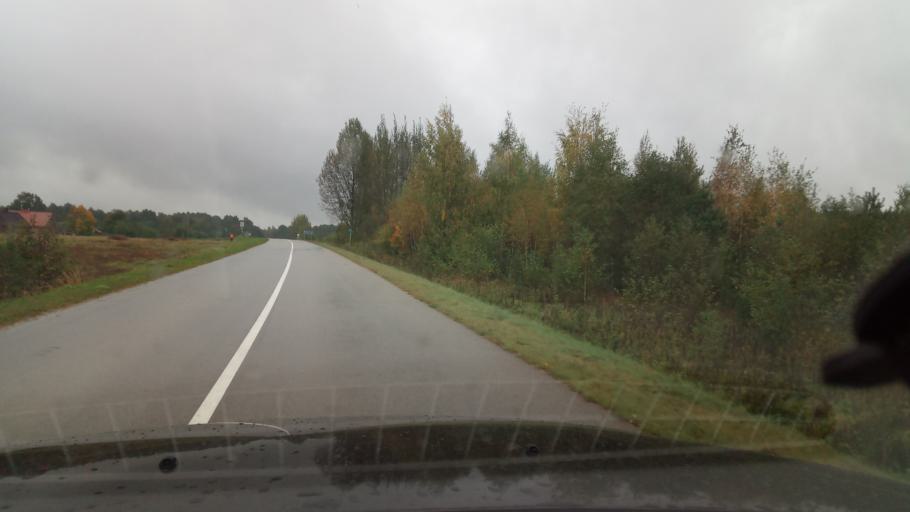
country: LT
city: Skaidiskes
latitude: 54.5598
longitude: 25.4974
